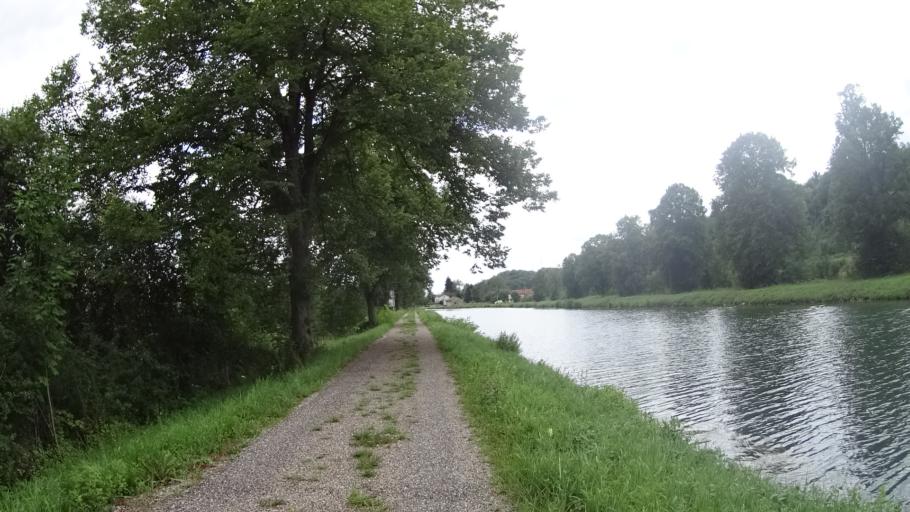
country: FR
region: Lorraine
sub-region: Departement de la Meuse
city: Commercy
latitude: 48.7591
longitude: 5.6021
